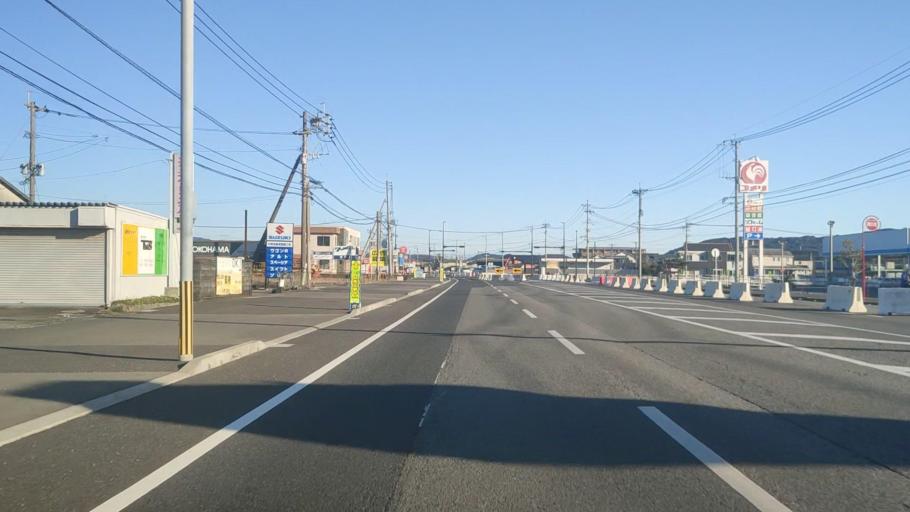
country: JP
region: Miyazaki
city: Nobeoka
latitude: 32.4005
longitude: 131.6304
